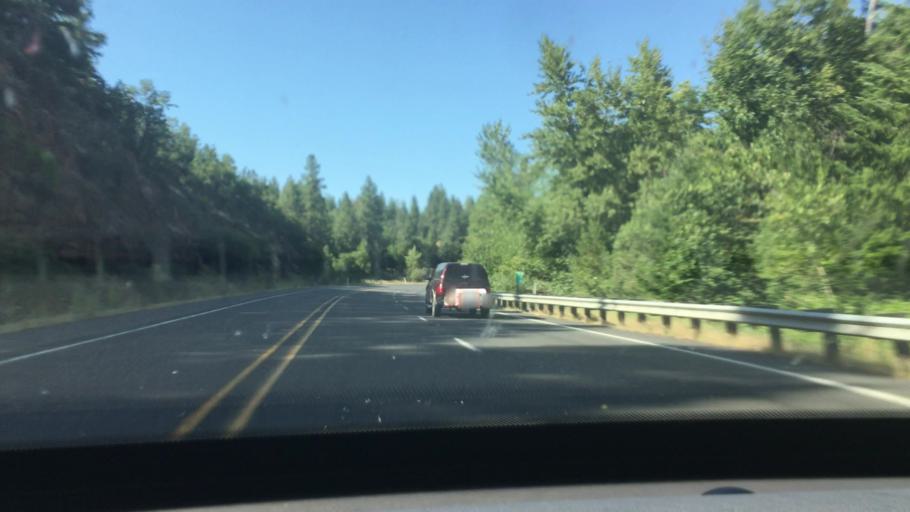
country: US
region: Washington
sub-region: Klickitat County
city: Goldendale
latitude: 45.8803
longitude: -120.7505
